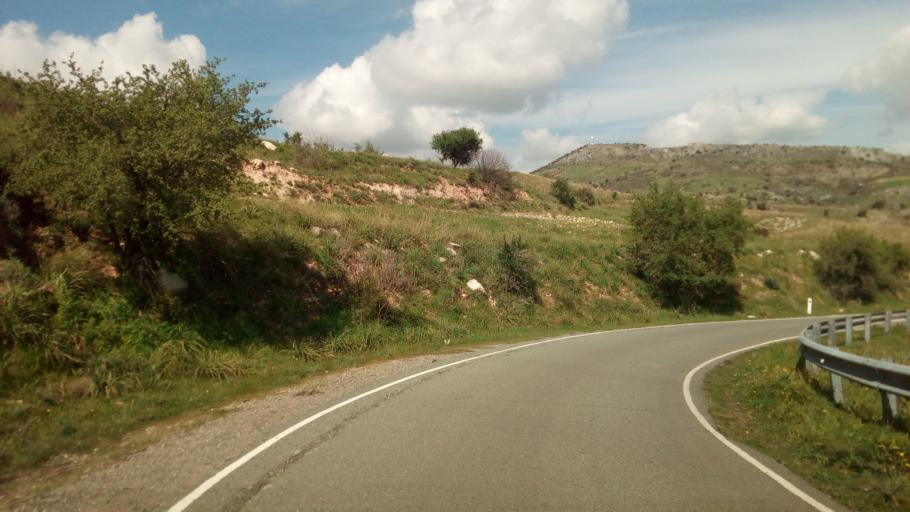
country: CY
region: Pafos
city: Mesogi
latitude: 34.7597
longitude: 32.5519
